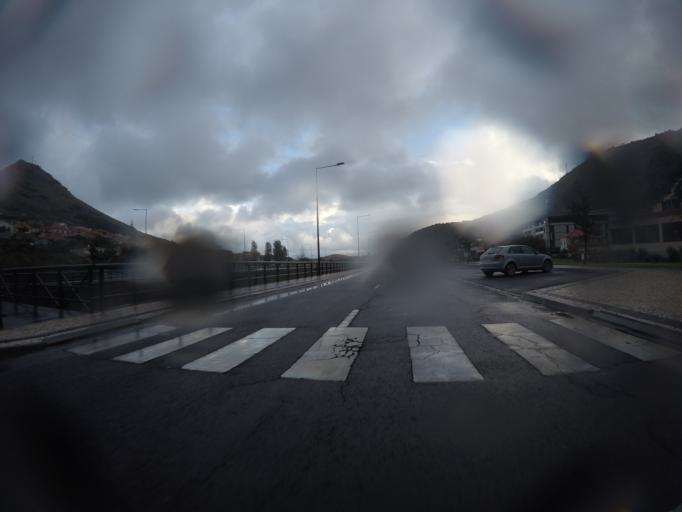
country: PT
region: Madeira
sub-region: Machico
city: Machico
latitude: 32.7231
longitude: -16.7697
